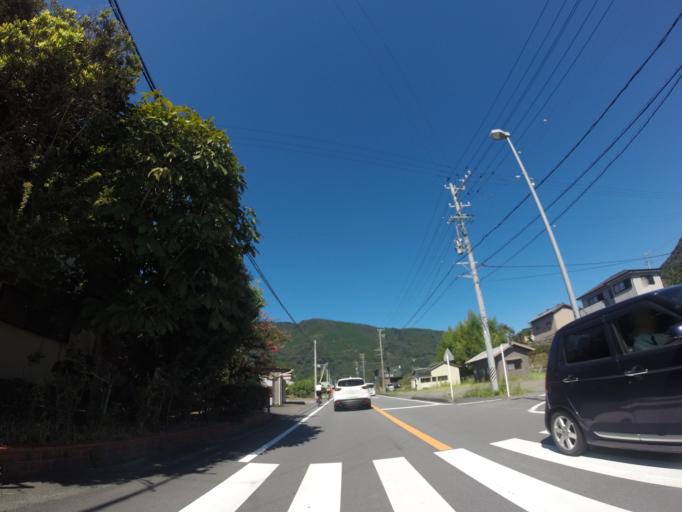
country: JP
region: Shizuoka
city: Kanaya
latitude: 34.8741
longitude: 138.1108
